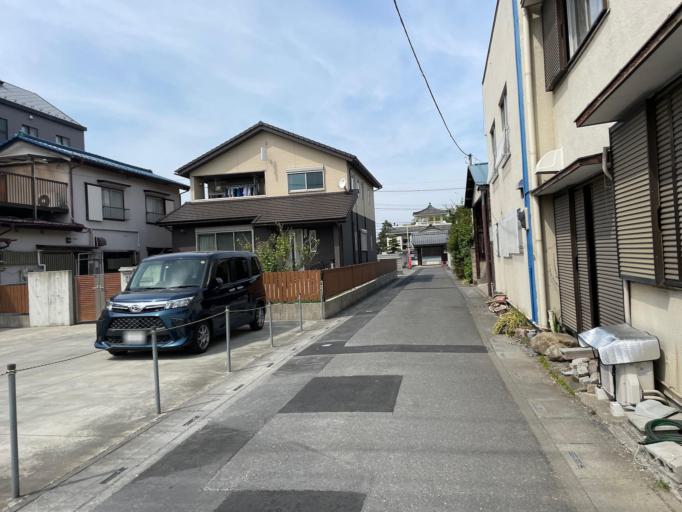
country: JP
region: Saitama
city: Fukayacho
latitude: 36.1947
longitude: 139.2887
